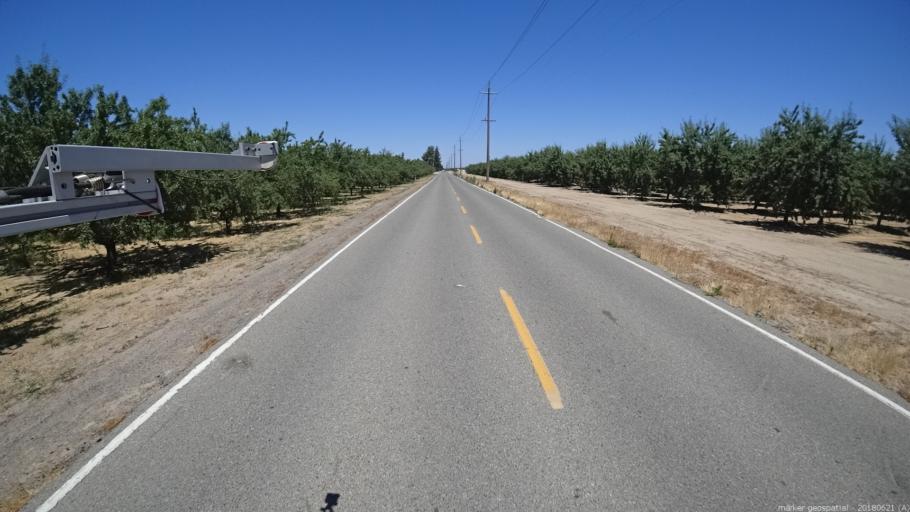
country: US
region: California
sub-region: Madera County
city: Bonadelle Ranchos-Madera Ranchos
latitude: 36.8709
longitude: -119.9113
